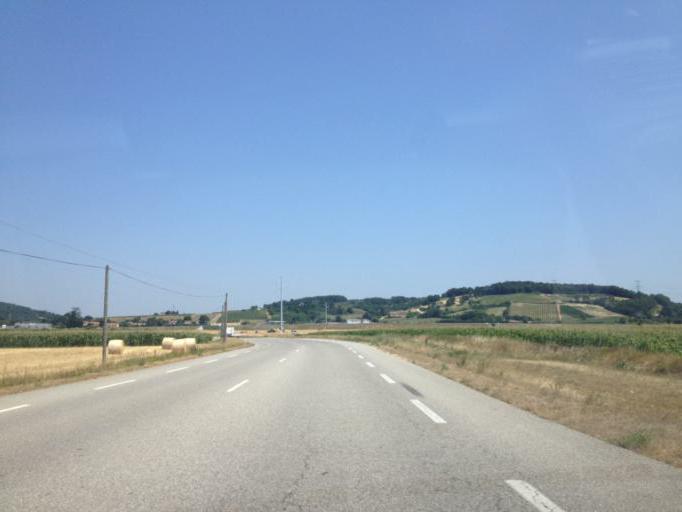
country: FR
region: Rhone-Alpes
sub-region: Departement de la Drome
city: Chanos-Curson
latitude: 45.0450
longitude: 4.9319
